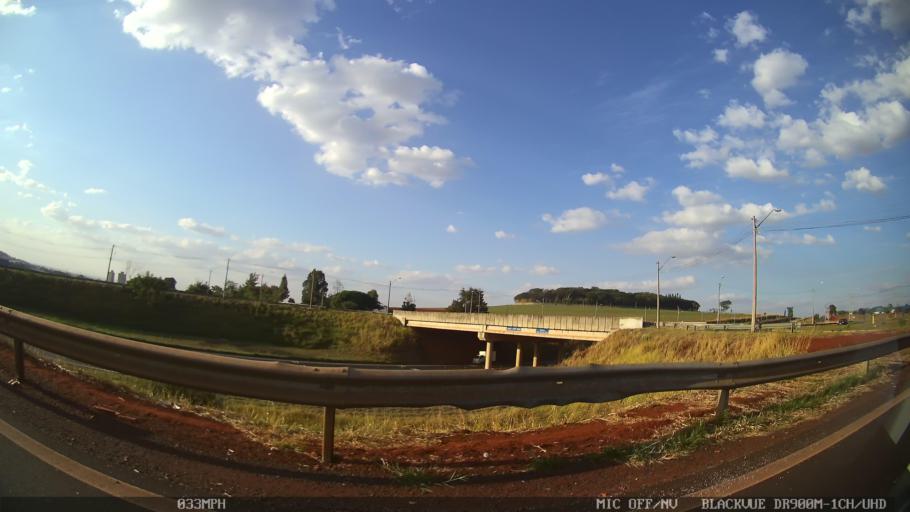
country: BR
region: Sao Paulo
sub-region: Ribeirao Preto
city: Ribeirao Preto
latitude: -21.2068
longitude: -47.7502
